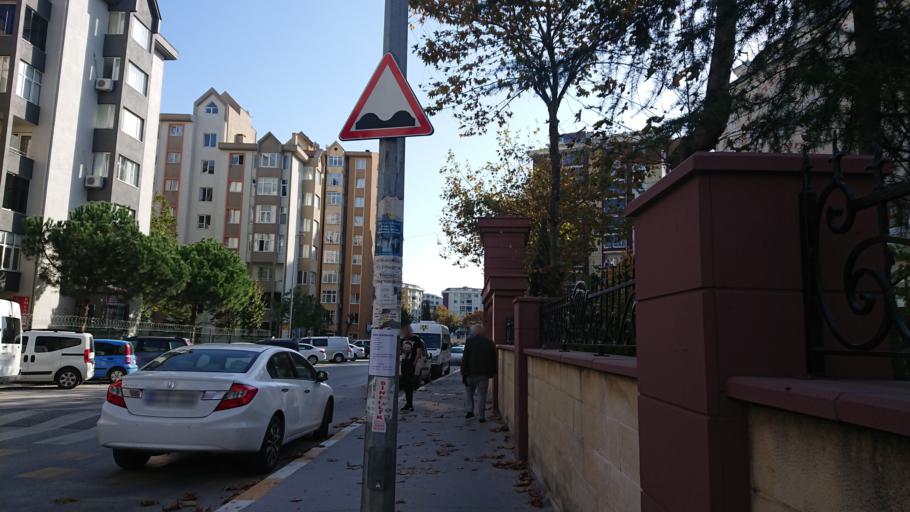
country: TR
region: Istanbul
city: Esenyurt
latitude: 41.0590
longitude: 28.6726
